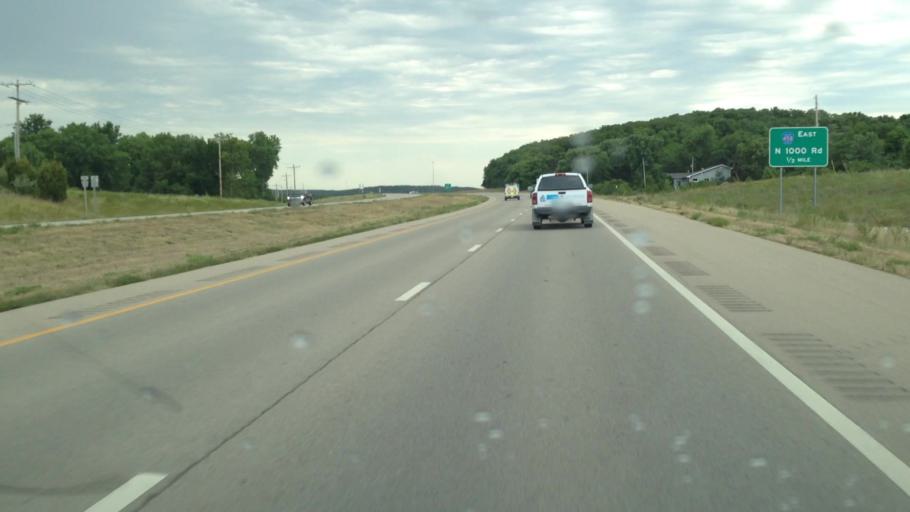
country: US
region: Kansas
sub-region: Douglas County
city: Lawrence
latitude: 38.8944
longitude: -95.2607
